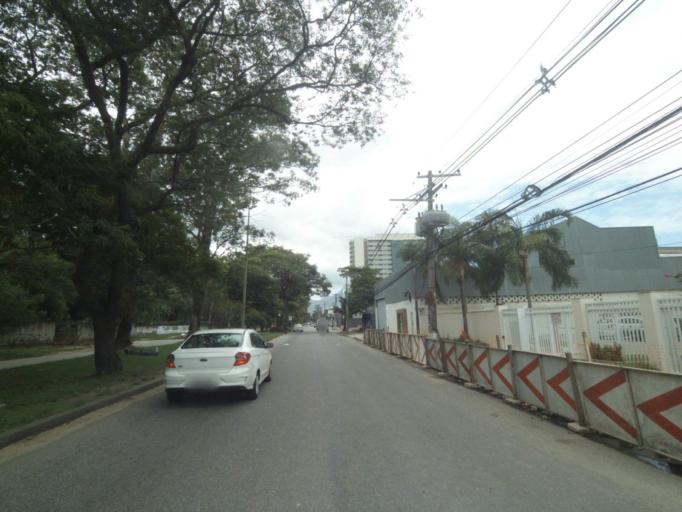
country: BR
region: Rio de Janeiro
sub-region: Nilopolis
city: Nilopolis
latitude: -22.9630
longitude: -43.4020
